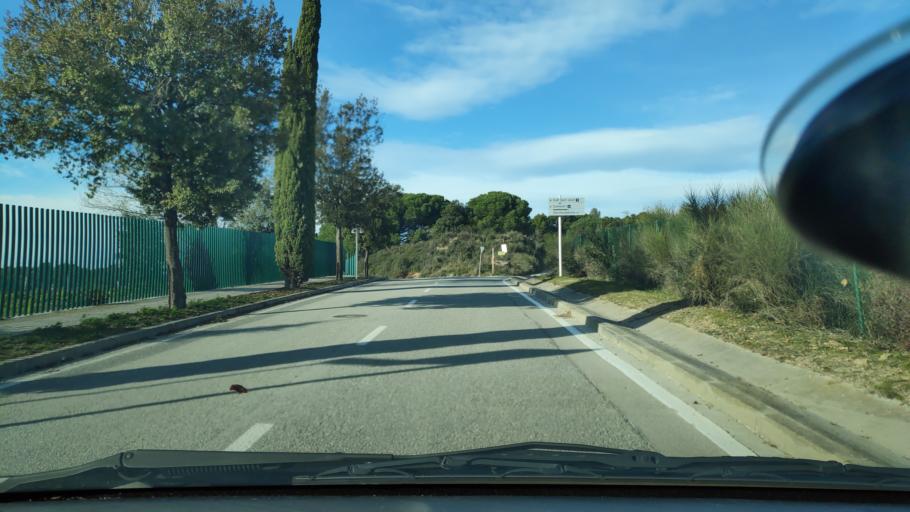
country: ES
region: Catalonia
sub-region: Provincia de Barcelona
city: Rubi
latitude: 41.4970
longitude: 2.0641
